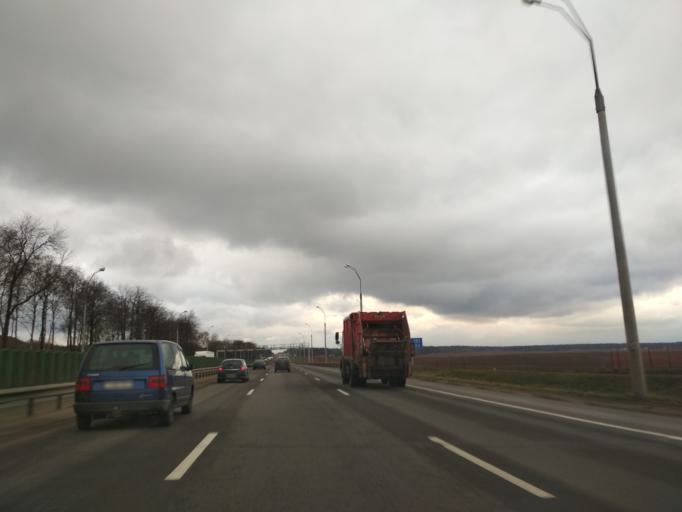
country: BY
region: Minsk
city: Vyaliki Trastsyanets
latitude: 53.8395
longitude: 27.7233
